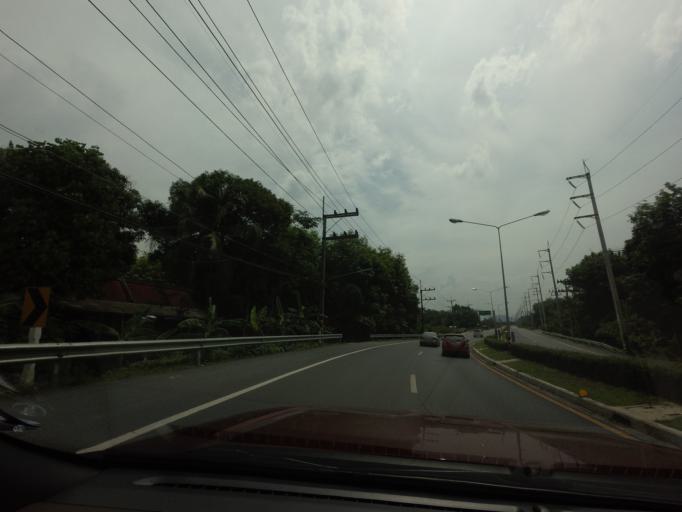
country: TH
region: Yala
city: Yala
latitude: 6.4982
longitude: 101.2819
